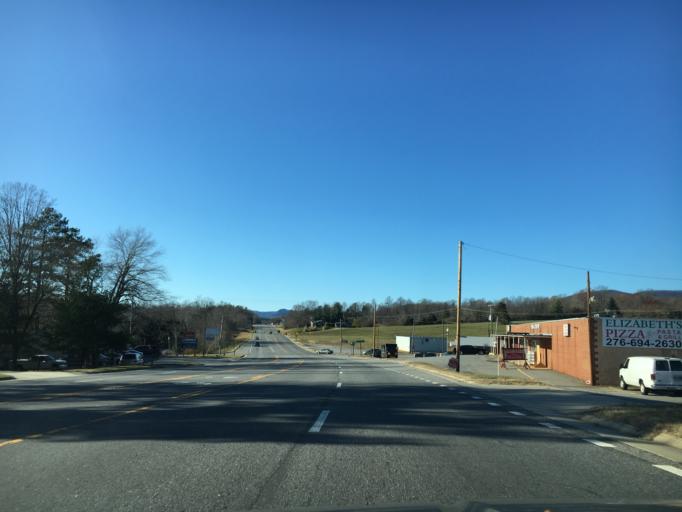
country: US
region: Virginia
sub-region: Patrick County
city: Patrick Springs
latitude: 36.6331
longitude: -80.1983
